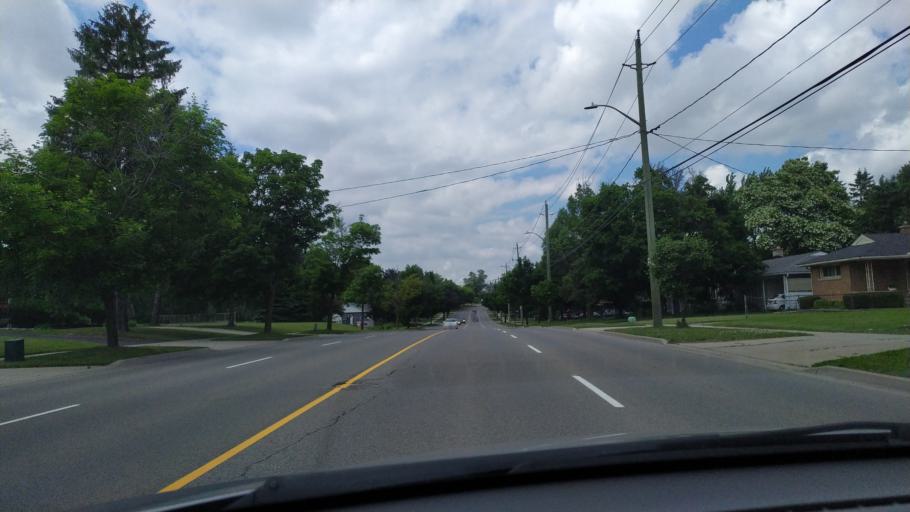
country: CA
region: Ontario
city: Kitchener
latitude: 43.4295
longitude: -80.5079
